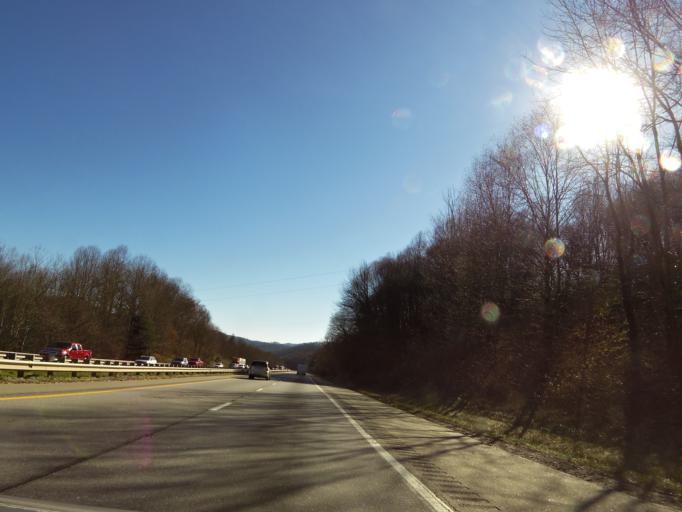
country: US
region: North Carolina
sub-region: Haywood County
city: Cove Creek
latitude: 35.5786
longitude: -82.9830
